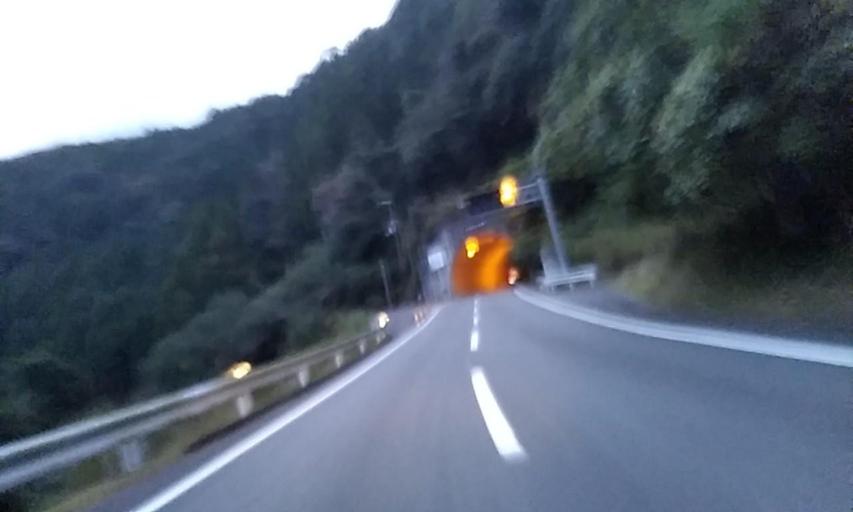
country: JP
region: Wakayama
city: Shingu
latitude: 33.7322
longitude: 135.9235
